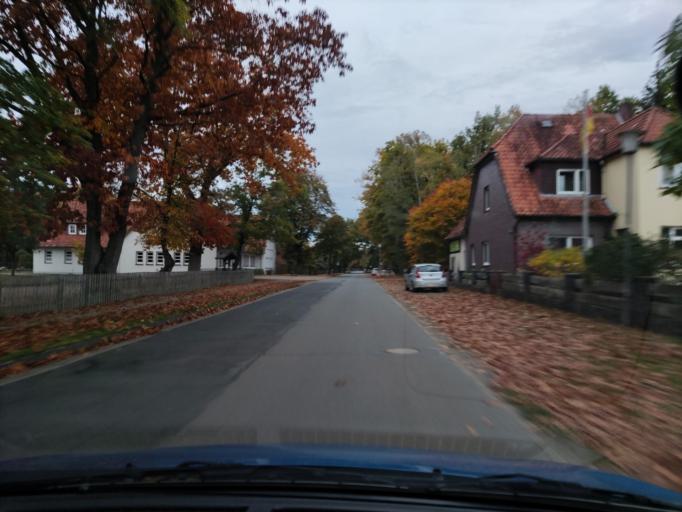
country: DE
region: Lower Saxony
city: Hermannsburg
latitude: 52.8710
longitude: 10.1221
